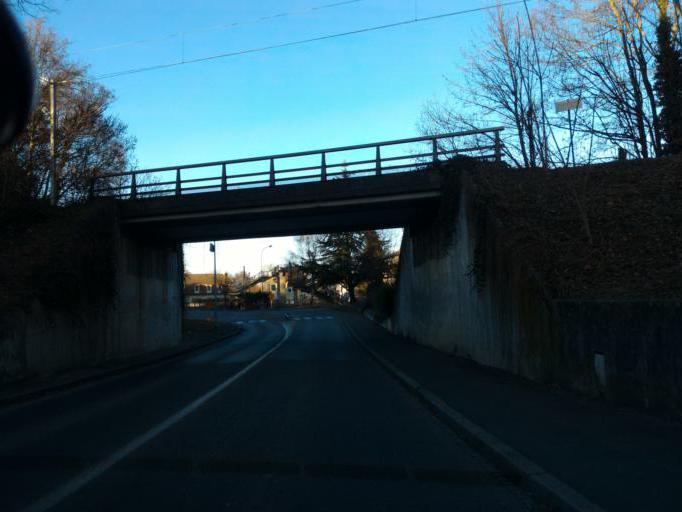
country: FR
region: Alsace
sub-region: Departement du Haut-Rhin
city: Riedisheim
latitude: 47.7538
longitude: 7.3686
